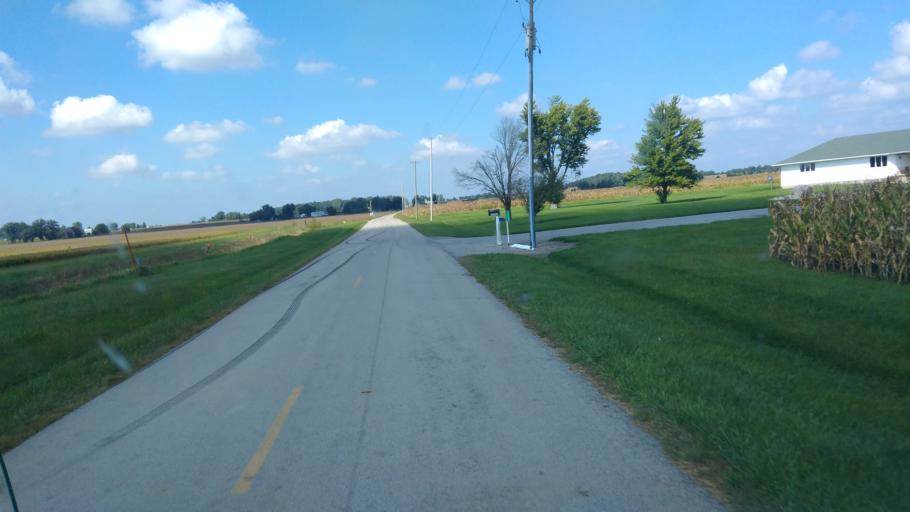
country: US
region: Ohio
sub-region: Logan County
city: Lakeview
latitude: 40.5926
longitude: -83.8799
